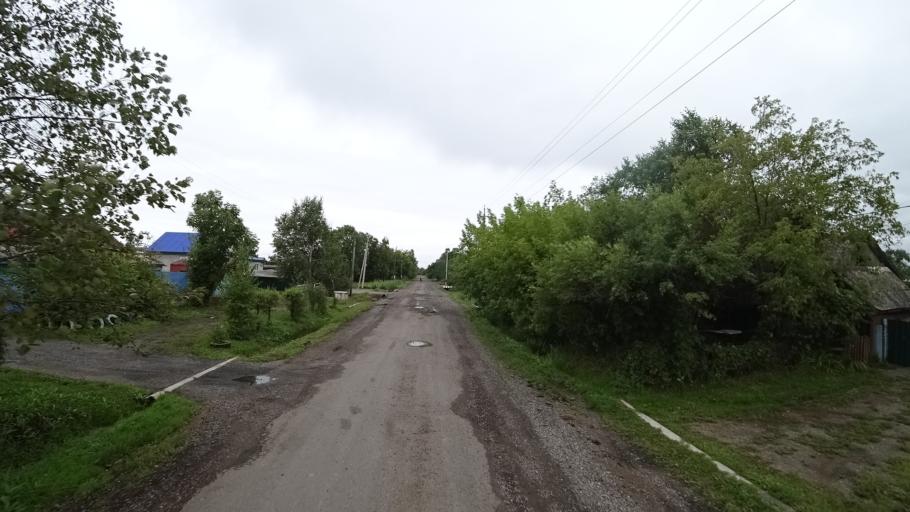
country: RU
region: Primorskiy
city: Chernigovka
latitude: 44.3475
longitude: 132.5776
